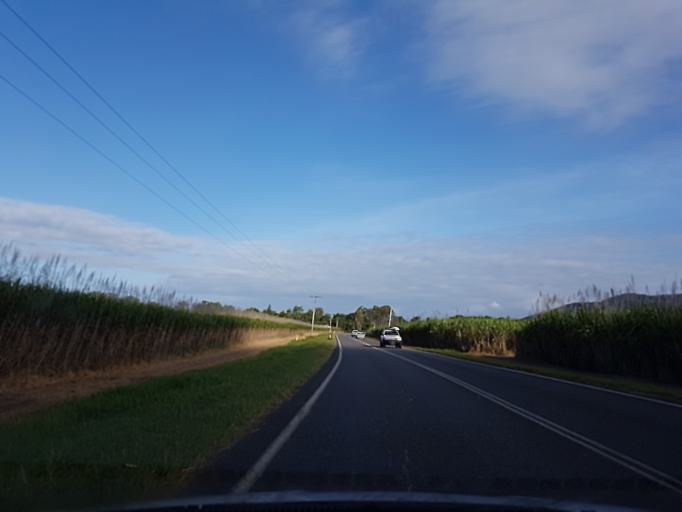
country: AU
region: Queensland
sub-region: Cairns
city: Port Douglas
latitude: -16.3328
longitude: 145.4094
